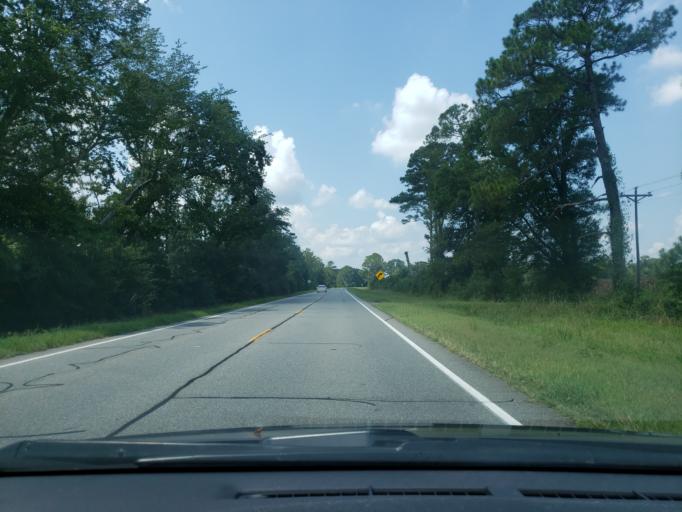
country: US
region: Georgia
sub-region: Bleckley County
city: Cochran
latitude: 32.4528
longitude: -83.2733
